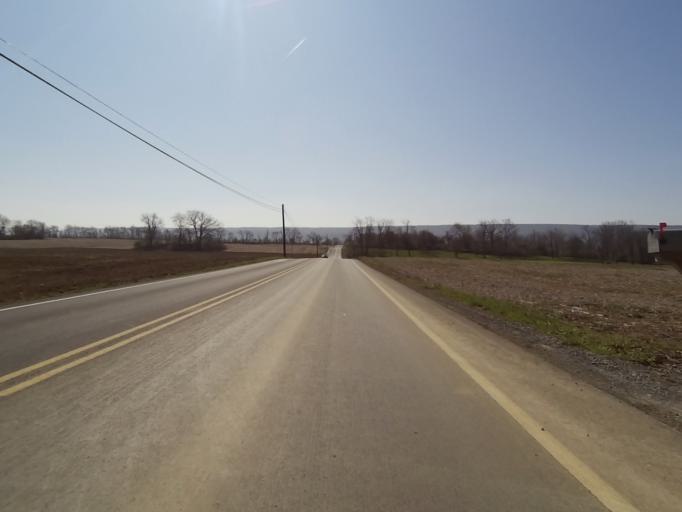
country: US
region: Pennsylvania
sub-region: Centre County
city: Pine Grove Mills
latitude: 40.7620
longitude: -77.9115
